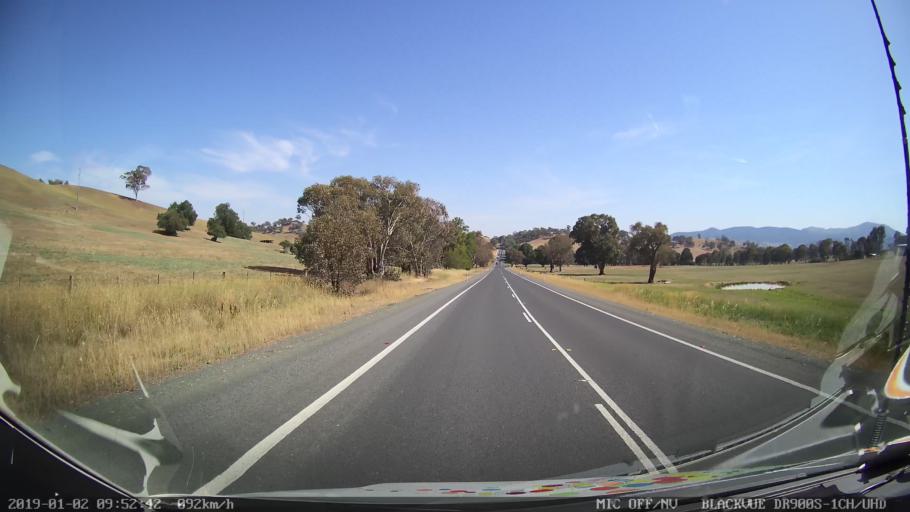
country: AU
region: New South Wales
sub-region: Tumut Shire
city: Tumut
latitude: -35.2576
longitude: 148.2044
